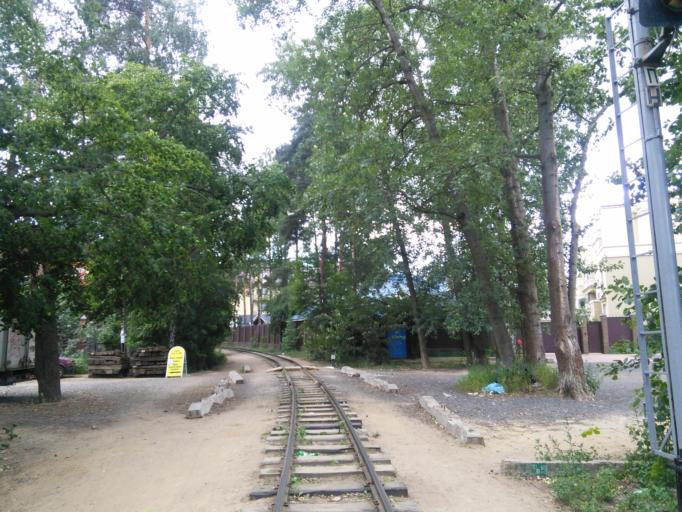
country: RU
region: St.-Petersburg
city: Kolomyagi
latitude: 60.0333
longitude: 30.2910
